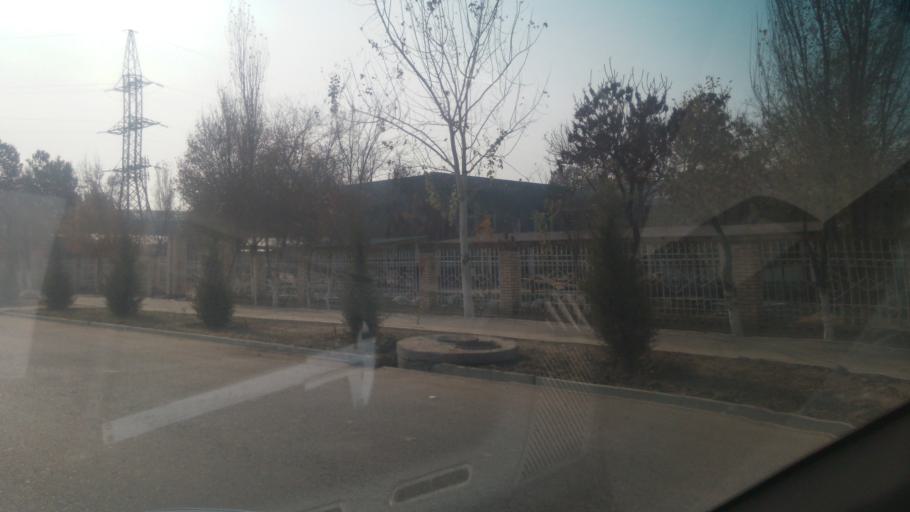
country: UZ
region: Sirdaryo
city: Guliston
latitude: 40.5130
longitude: 68.7701
